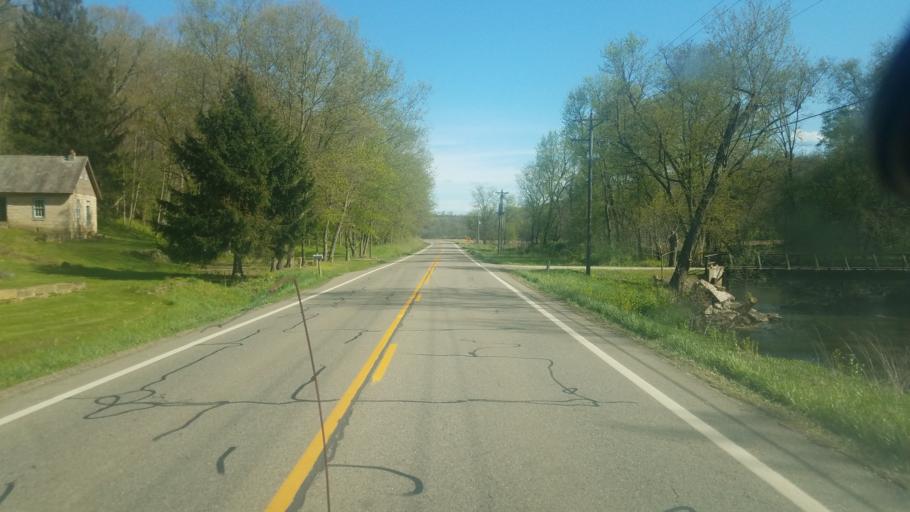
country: US
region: Ohio
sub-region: Coshocton County
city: Coshocton
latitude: 40.3398
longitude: -81.8811
